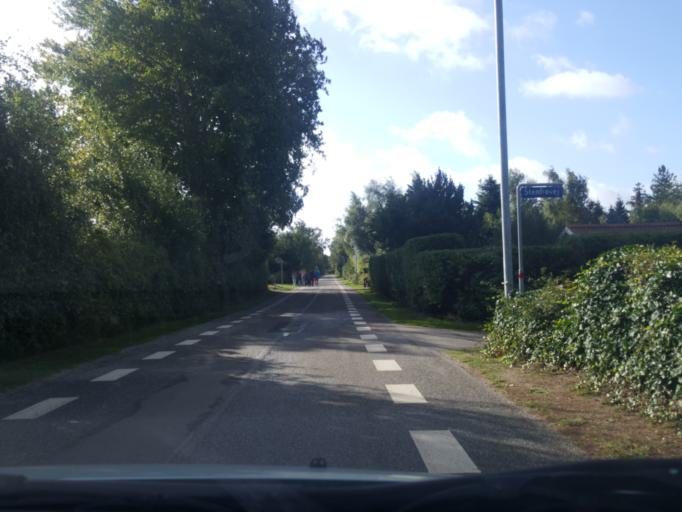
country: DK
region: Zealand
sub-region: Guldborgsund Kommune
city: Nykobing Falster
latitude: 54.6548
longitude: 11.9567
